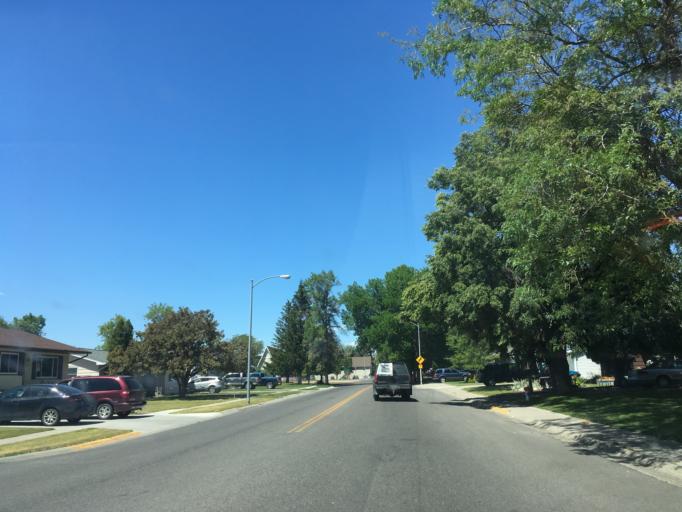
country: US
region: Montana
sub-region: Yellowstone County
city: Billings
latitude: 45.7712
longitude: -108.5647
